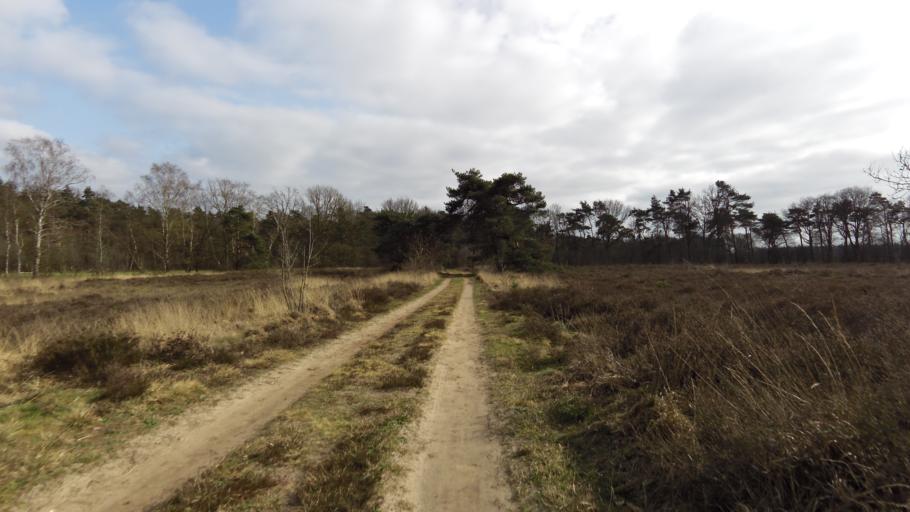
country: NL
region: Gelderland
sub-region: Gemeente Barneveld
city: Voorthuizen
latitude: 52.2077
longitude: 5.6038
